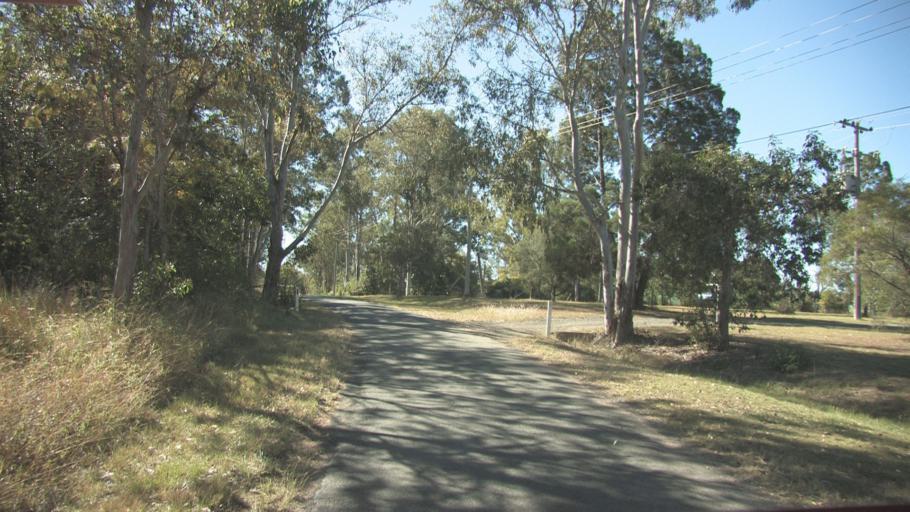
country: AU
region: Queensland
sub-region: Logan
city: North Maclean
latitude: -27.7670
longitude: 153.0293
